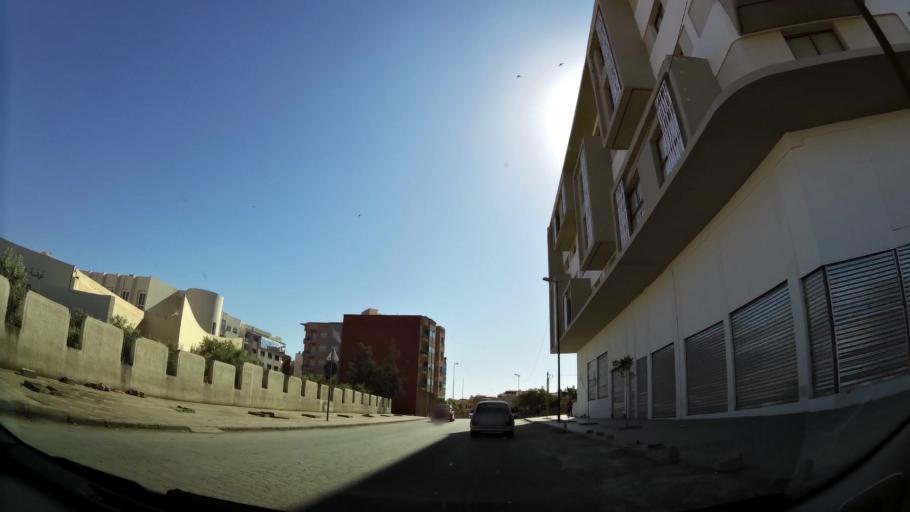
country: MA
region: Oriental
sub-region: Oujda-Angad
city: Oujda
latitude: 34.6562
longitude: -1.8995
